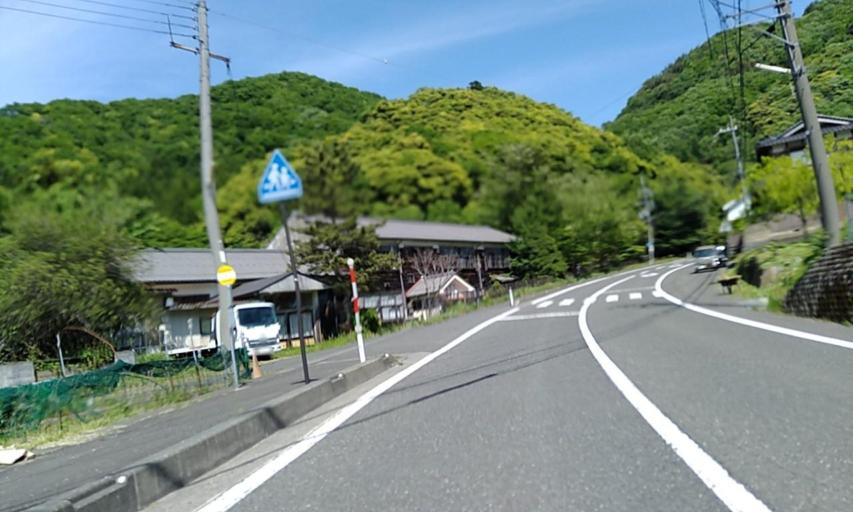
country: JP
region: Fukui
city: Obama
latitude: 35.5331
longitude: 135.7699
